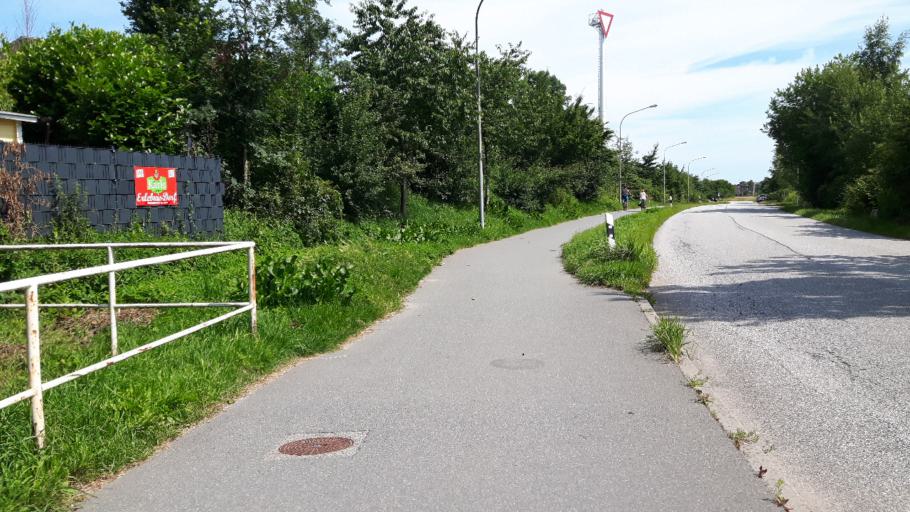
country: DE
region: Schleswig-Holstein
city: Travemuende
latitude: 53.9553
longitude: 10.8543
